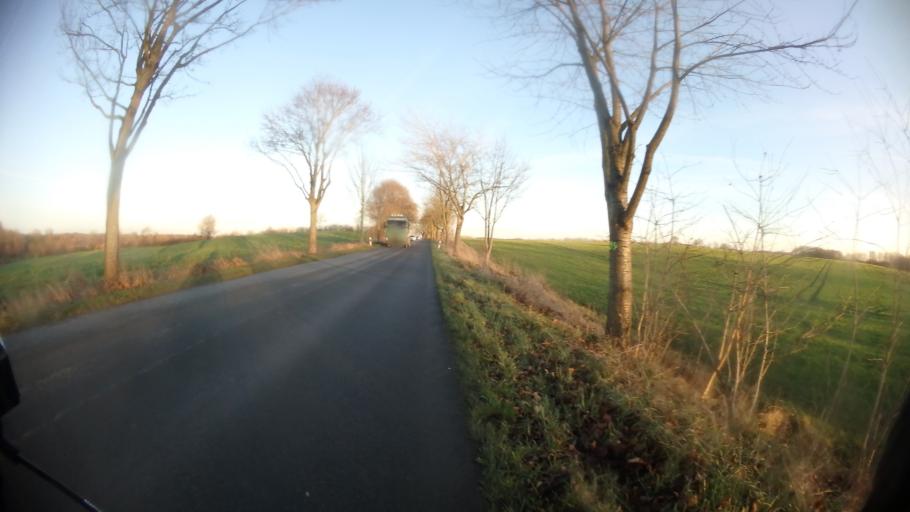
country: DE
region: Schleswig-Holstein
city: Scharbeutz
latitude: 54.0167
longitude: 10.7138
